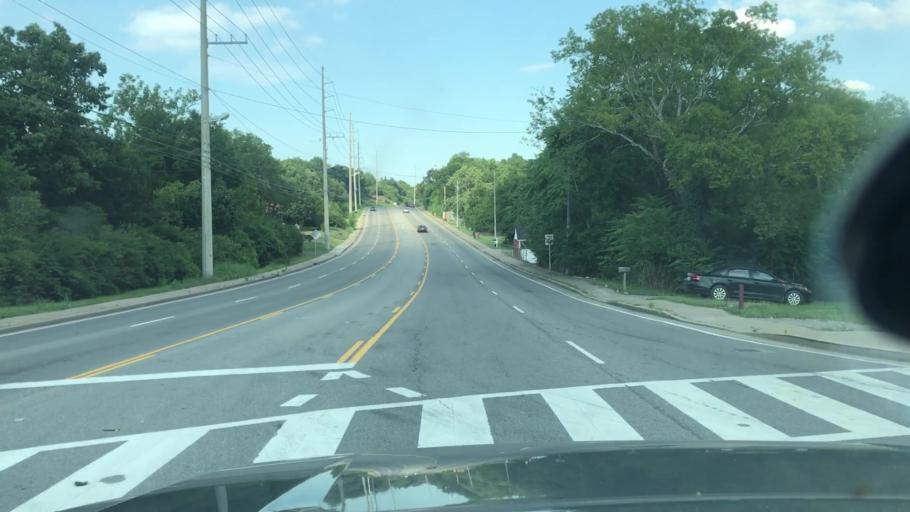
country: US
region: Tennessee
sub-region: Davidson County
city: Nashville
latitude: 36.2061
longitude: -86.8108
